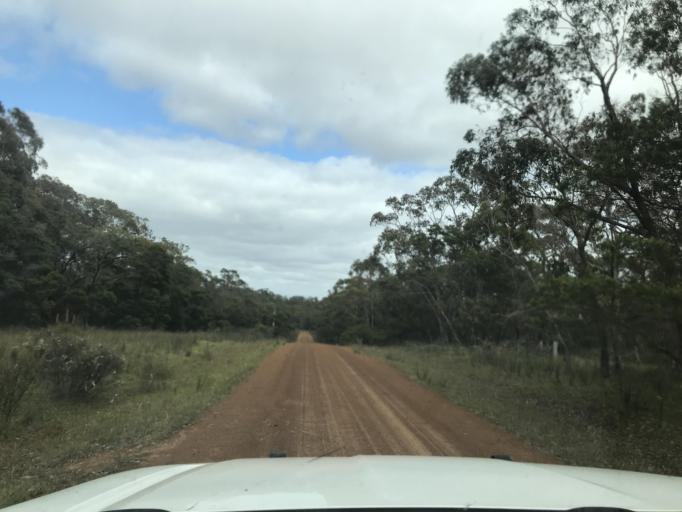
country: AU
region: South Australia
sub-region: Wattle Range
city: Penola
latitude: -37.3344
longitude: 141.4140
